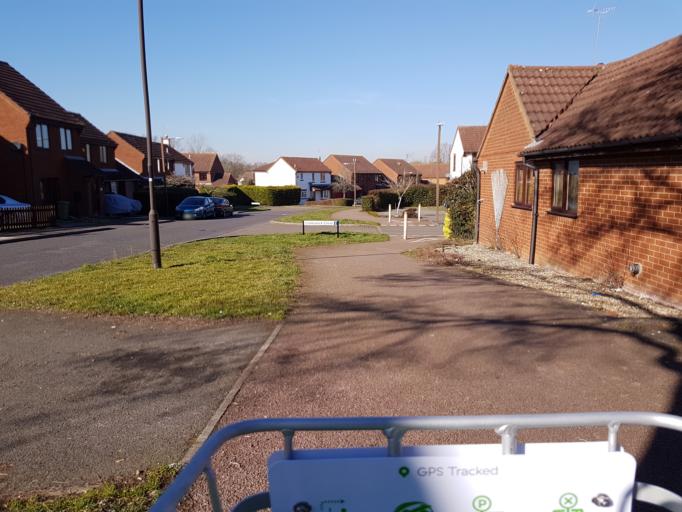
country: GB
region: England
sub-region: Buckinghamshire
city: Newton Longville
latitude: 52.0025
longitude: -0.7677
